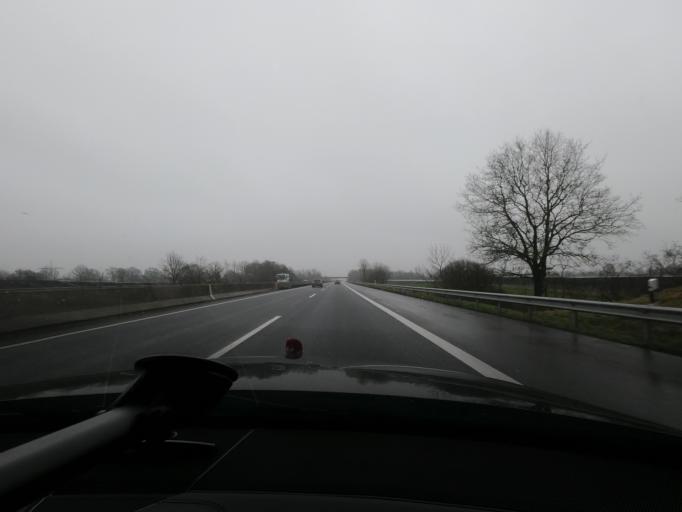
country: DE
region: Schleswig-Holstein
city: Bokel
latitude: 54.2539
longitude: 9.8064
